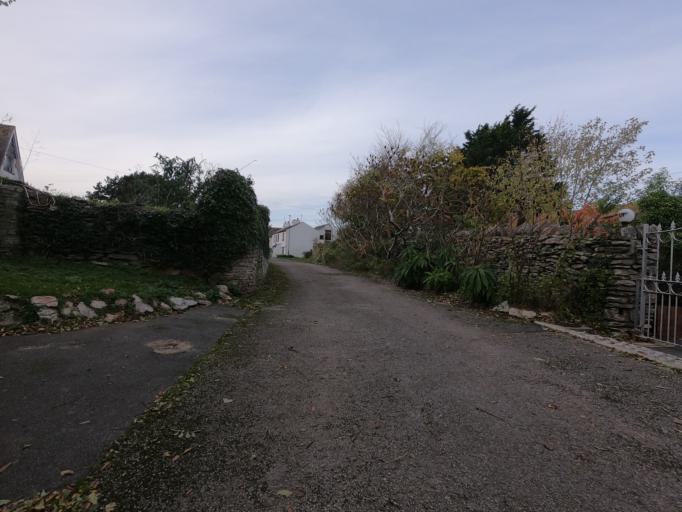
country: GB
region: England
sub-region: Borough of Torbay
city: Brixham
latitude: 50.3982
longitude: -3.4977
